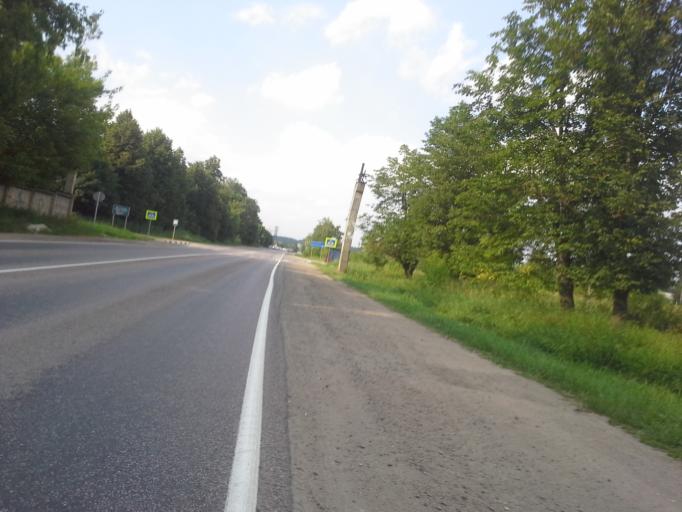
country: RU
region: Moskovskaya
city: Istra
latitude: 55.9033
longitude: 36.8079
